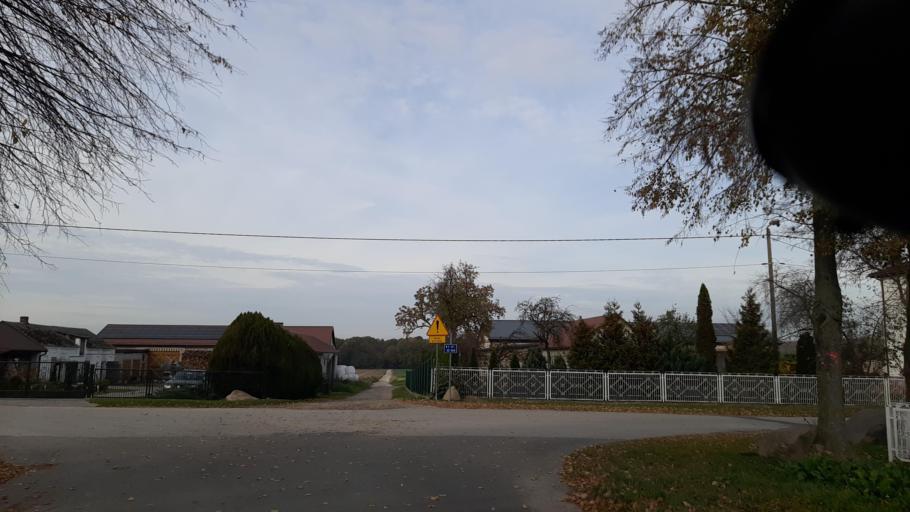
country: PL
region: Lublin Voivodeship
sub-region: Powiat lubelski
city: Garbow
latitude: 51.3883
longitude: 22.3691
